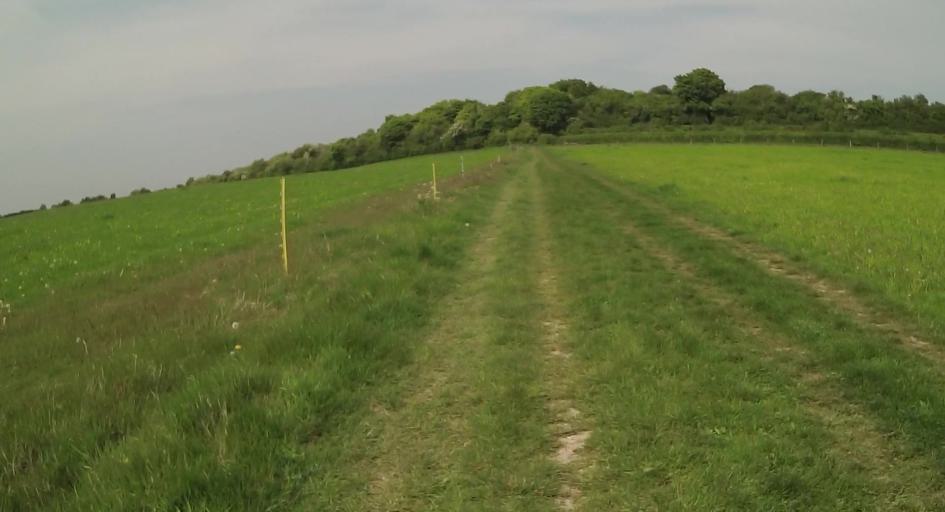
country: GB
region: England
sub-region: Hampshire
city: Kingsclere
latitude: 51.3172
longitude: -1.2333
